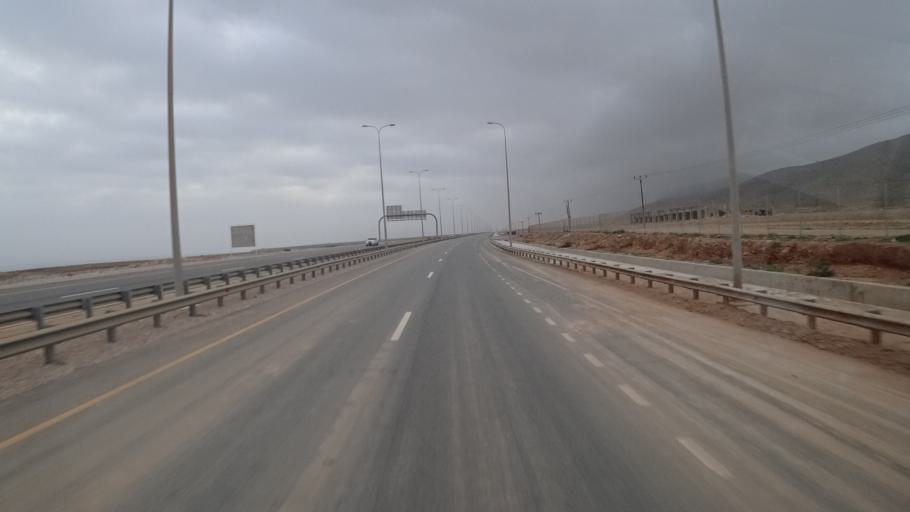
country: OM
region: Zufar
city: Salalah
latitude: 17.0307
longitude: 54.6038
